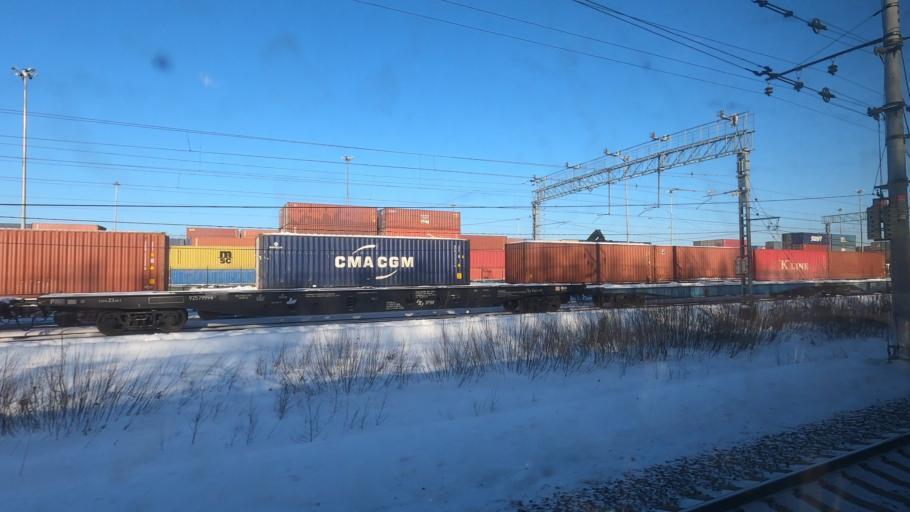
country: RU
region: Moskovskaya
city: Elektrougli
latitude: 55.7233
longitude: 38.2366
